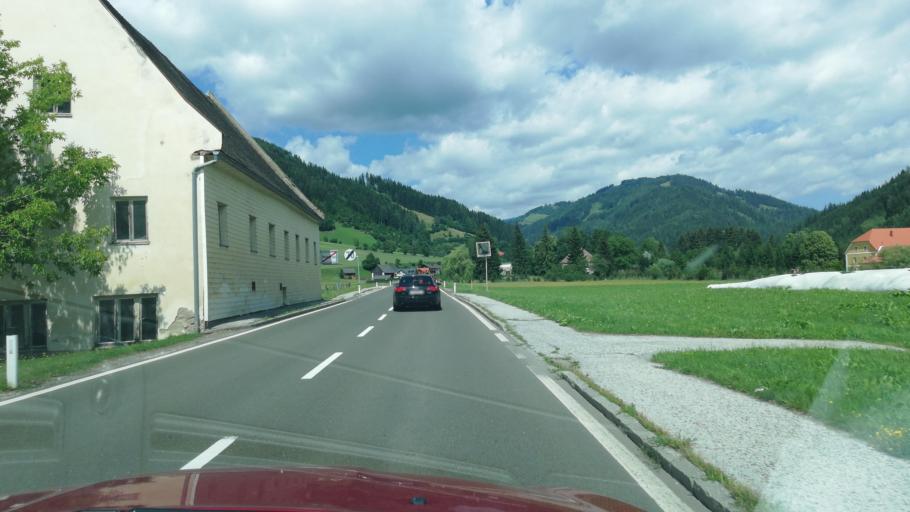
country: AT
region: Styria
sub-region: Politischer Bezirk Murtal
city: Oberzeiring
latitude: 47.2721
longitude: 14.4851
